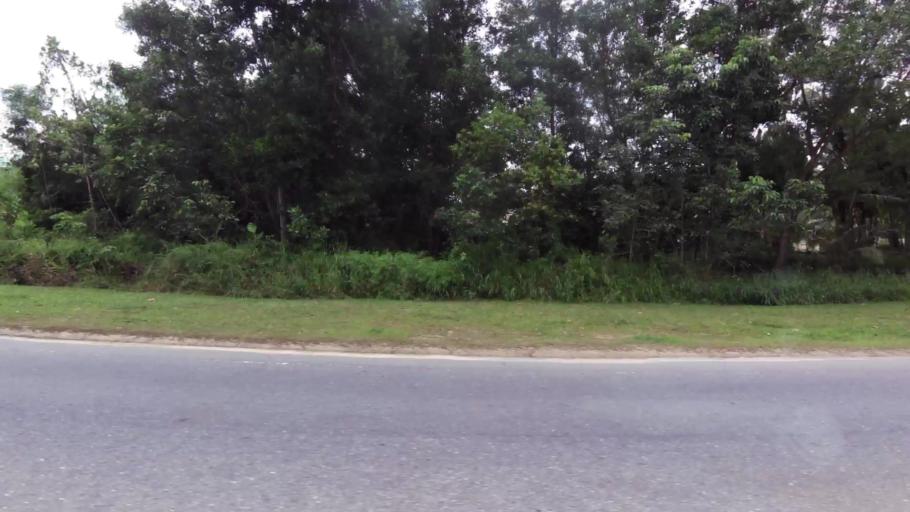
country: BN
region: Brunei and Muara
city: Bandar Seri Begawan
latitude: 4.8872
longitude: 114.9108
